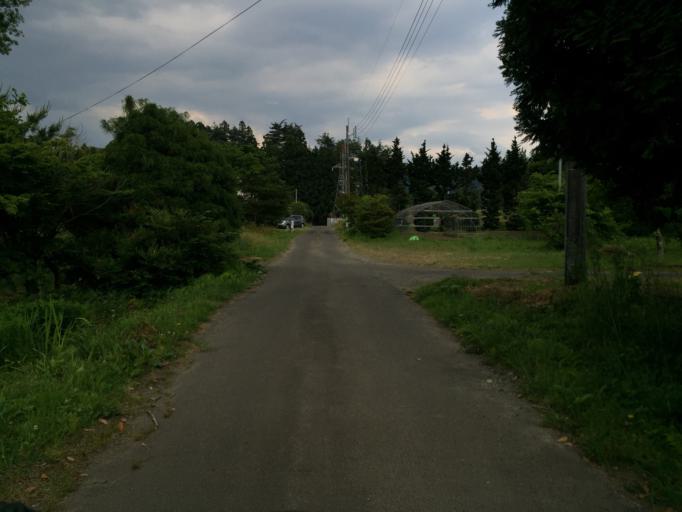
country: JP
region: Fukushima
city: Fukushima-shi
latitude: 37.7064
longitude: 140.3465
